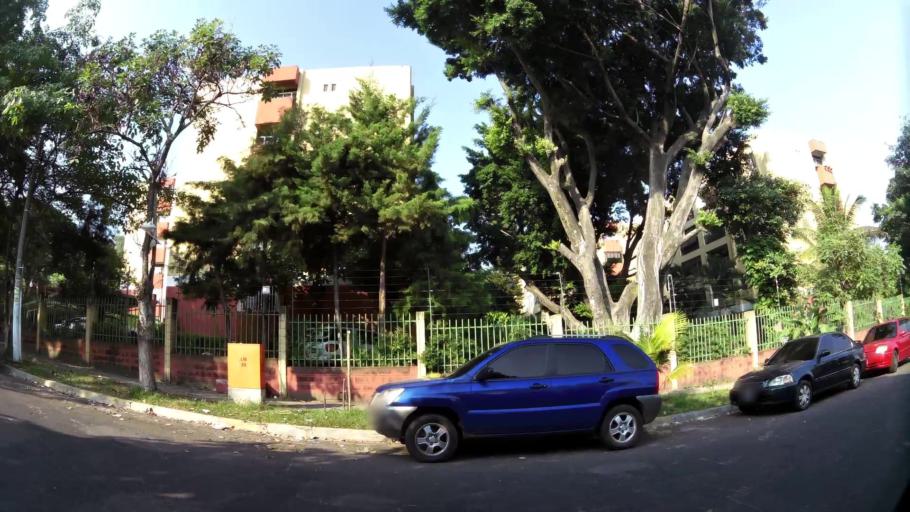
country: SV
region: San Salvador
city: San Salvador
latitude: 13.6820
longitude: -89.2189
